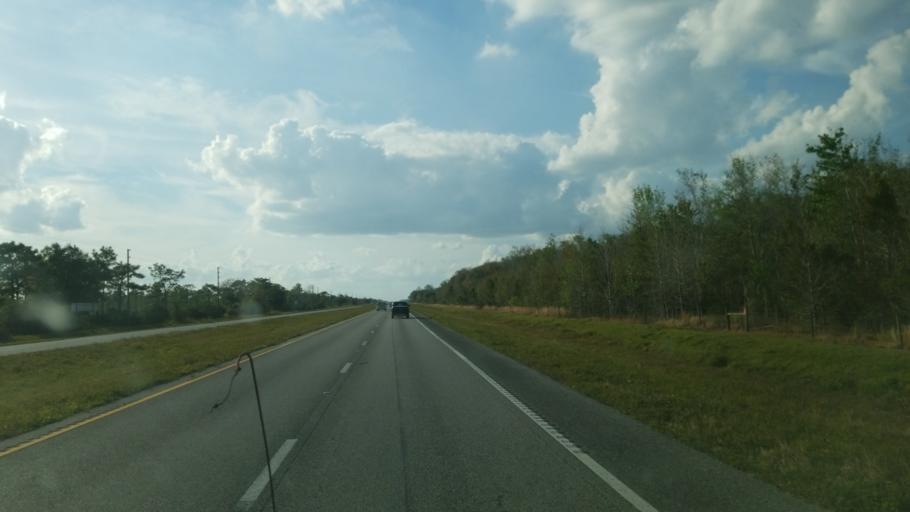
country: US
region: Florida
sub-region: Osceola County
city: Saint Cloud
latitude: 28.1339
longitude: -81.0211
